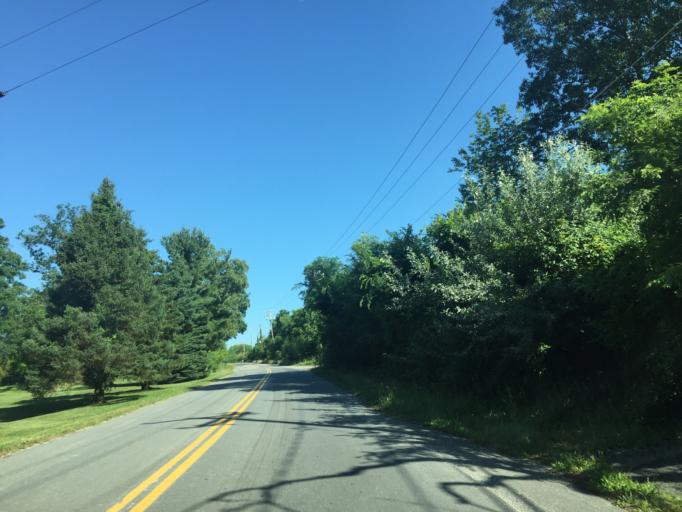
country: US
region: Maryland
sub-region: Harford County
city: Joppatowne
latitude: 39.4614
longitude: -76.3622
